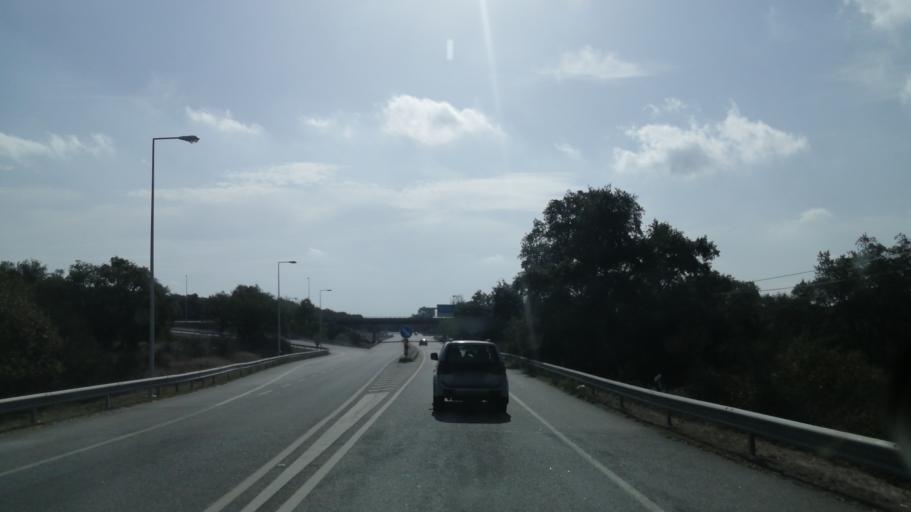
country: PT
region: Evora
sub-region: Evora
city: Evora
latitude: 38.5966
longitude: -8.0254
